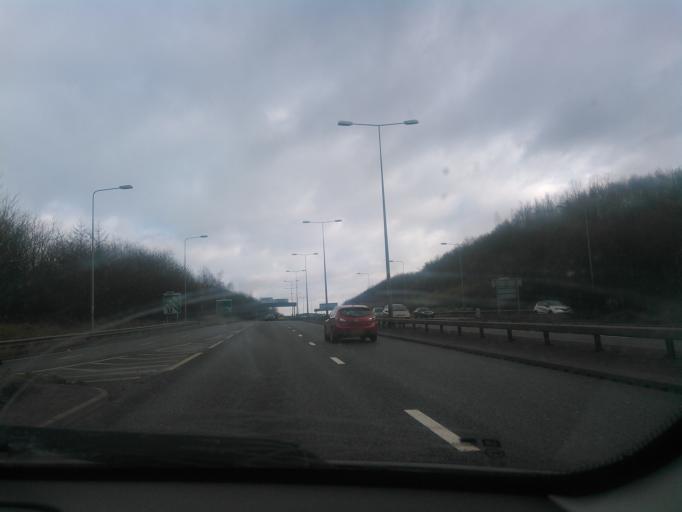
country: GB
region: England
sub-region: Staffordshire
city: Longton
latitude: 52.9914
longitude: -2.1553
